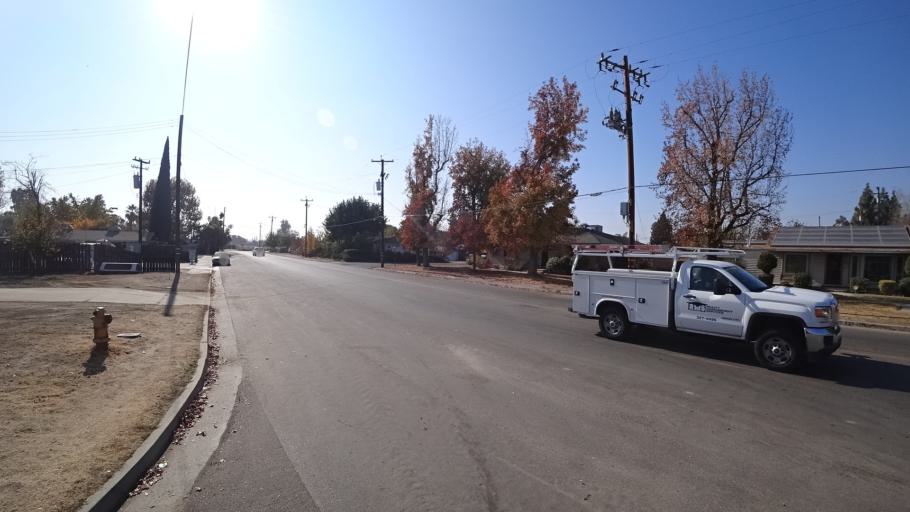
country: US
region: California
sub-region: Kern County
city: Bakersfield
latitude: 35.3516
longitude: -119.0300
